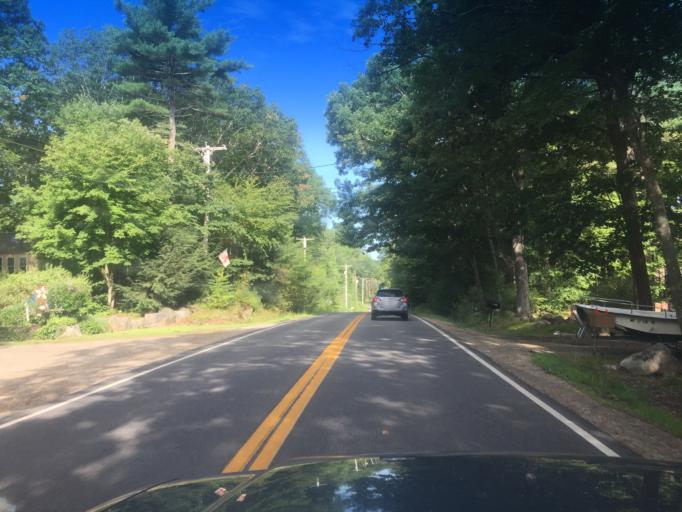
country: US
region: Maine
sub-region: York County
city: Eliot
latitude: 43.1974
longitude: -70.7568
